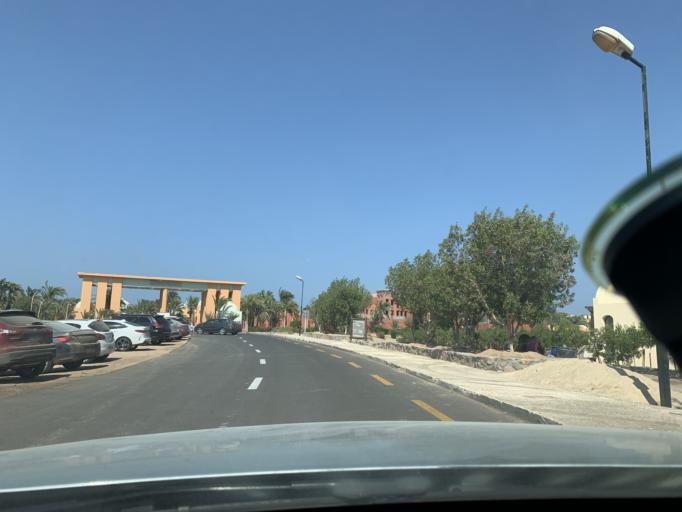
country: EG
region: Red Sea
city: El Gouna
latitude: 27.4033
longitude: 33.6756
